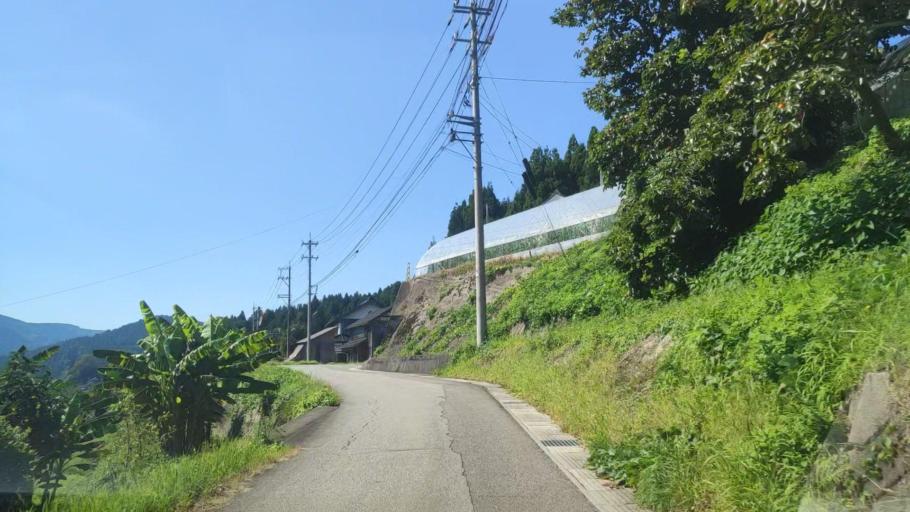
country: JP
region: Ishikawa
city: Nanao
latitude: 37.3706
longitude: 136.8700
